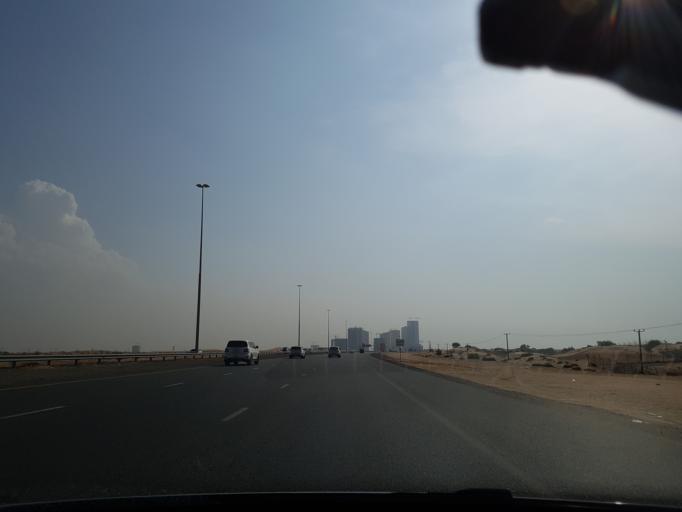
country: AE
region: Ajman
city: Ajman
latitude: 25.4144
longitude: 55.5874
